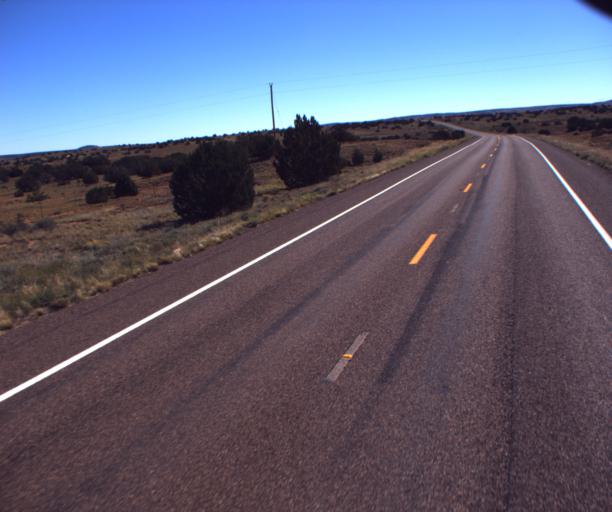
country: US
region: Arizona
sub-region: Apache County
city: Saint Johns
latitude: 34.5990
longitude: -109.6356
